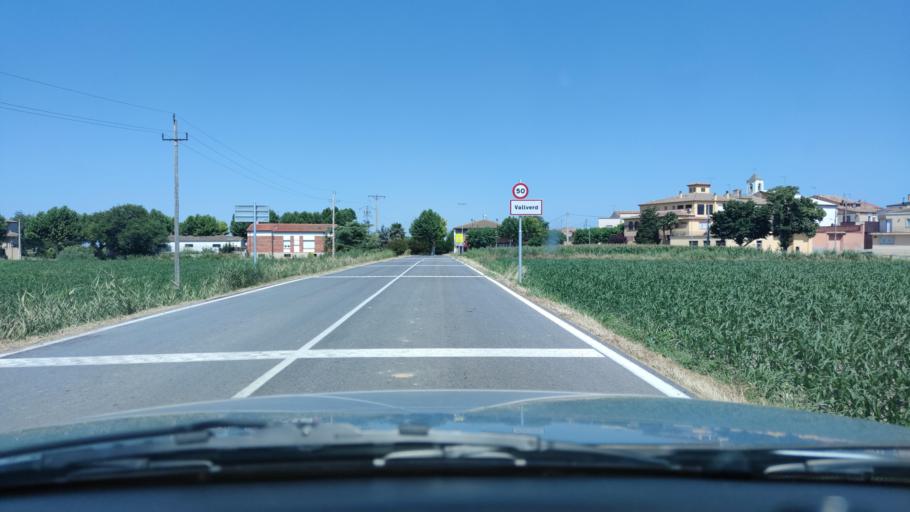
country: ES
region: Catalonia
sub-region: Provincia de Lleida
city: Linyola
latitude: 41.6954
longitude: 0.9523
